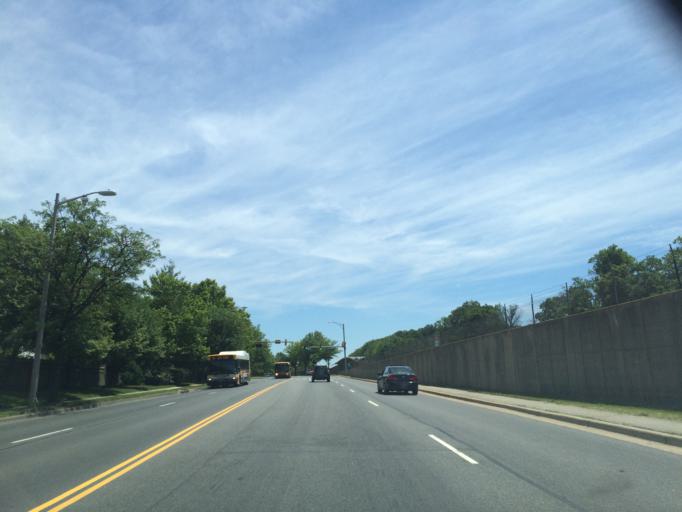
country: US
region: Virginia
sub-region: Fairfax County
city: Franconia
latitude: 38.7990
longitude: -77.1323
